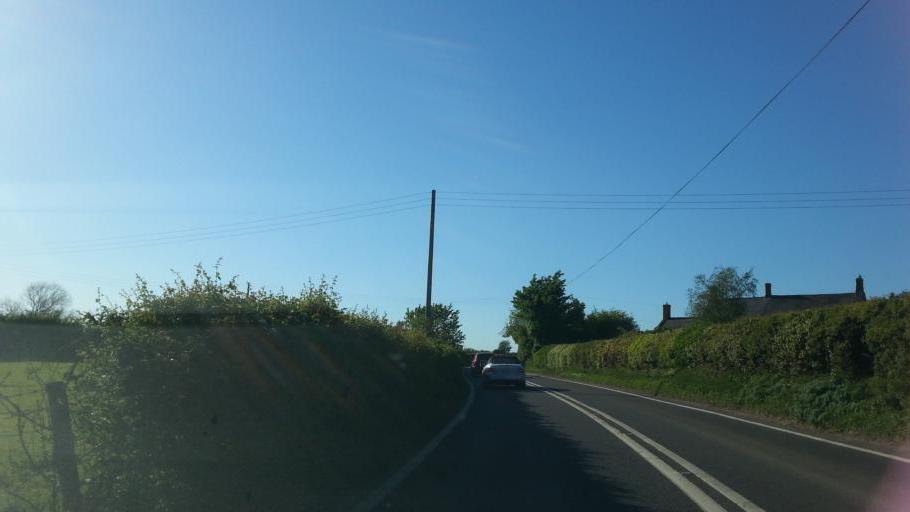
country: GB
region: England
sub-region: Somerset
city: Evercreech
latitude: 51.1398
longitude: -2.5168
